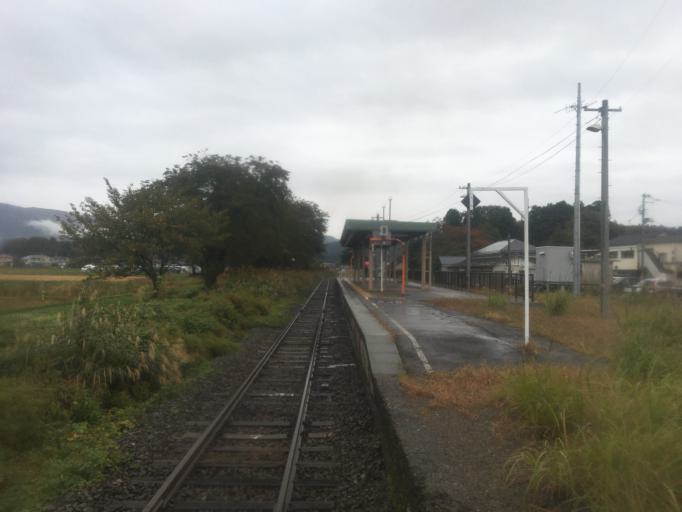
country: JP
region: Yamagata
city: Tsuruoka
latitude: 38.7938
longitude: 139.9768
